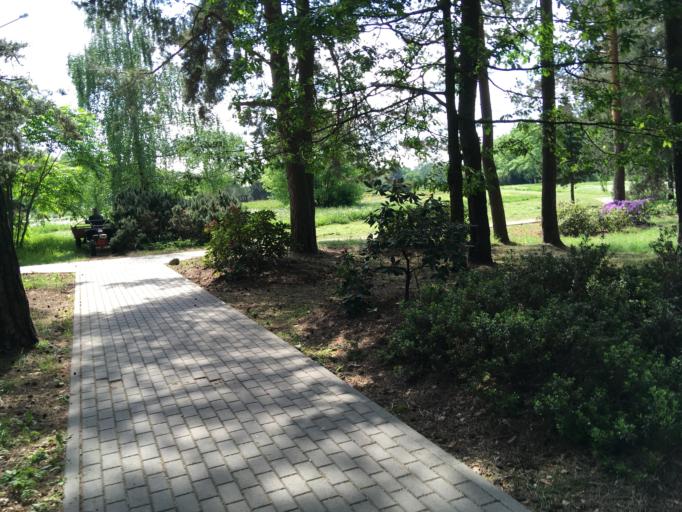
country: BY
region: Minsk
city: Minsk
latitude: 53.9209
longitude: 27.6103
